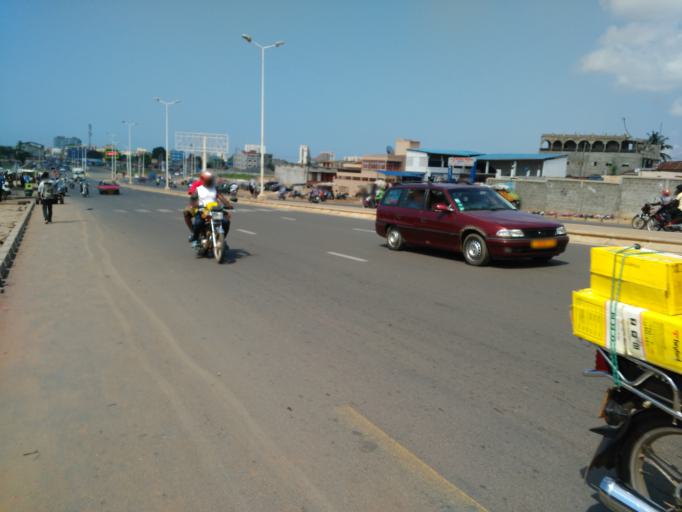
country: TG
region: Maritime
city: Lome
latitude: 6.1478
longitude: 1.2298
